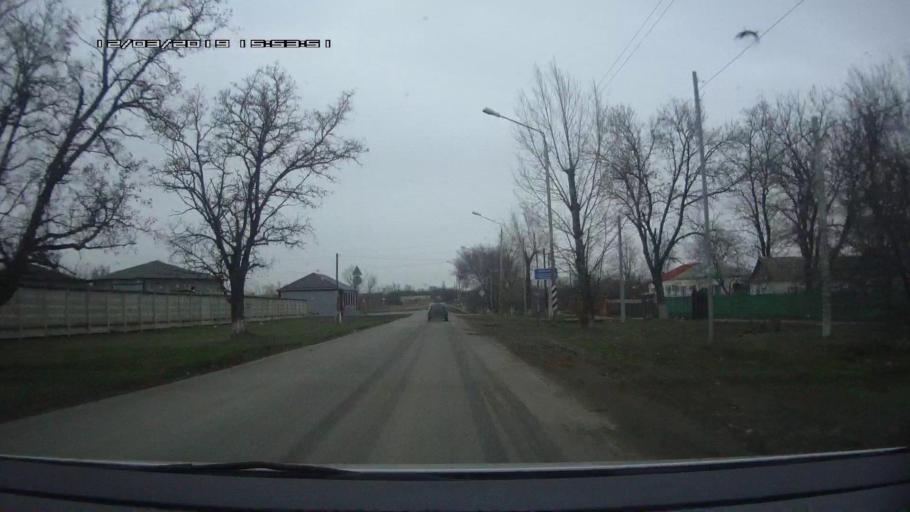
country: RU
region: Rostov
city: Novobataysk
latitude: 46.8872
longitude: 39.7767
